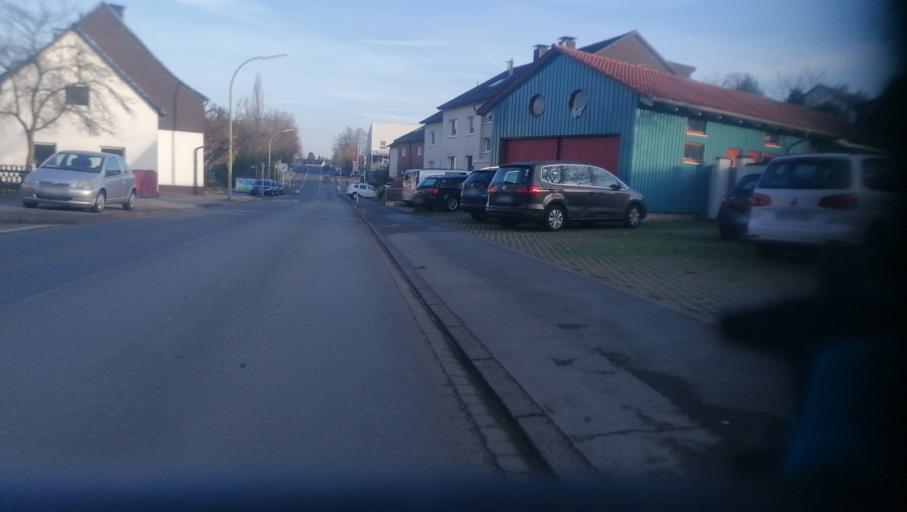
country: DE
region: North Rhine-Westphalia
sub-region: Regierungsbezirk Arnsberg
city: Dortmund
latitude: 51.4762
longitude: 7.4772
